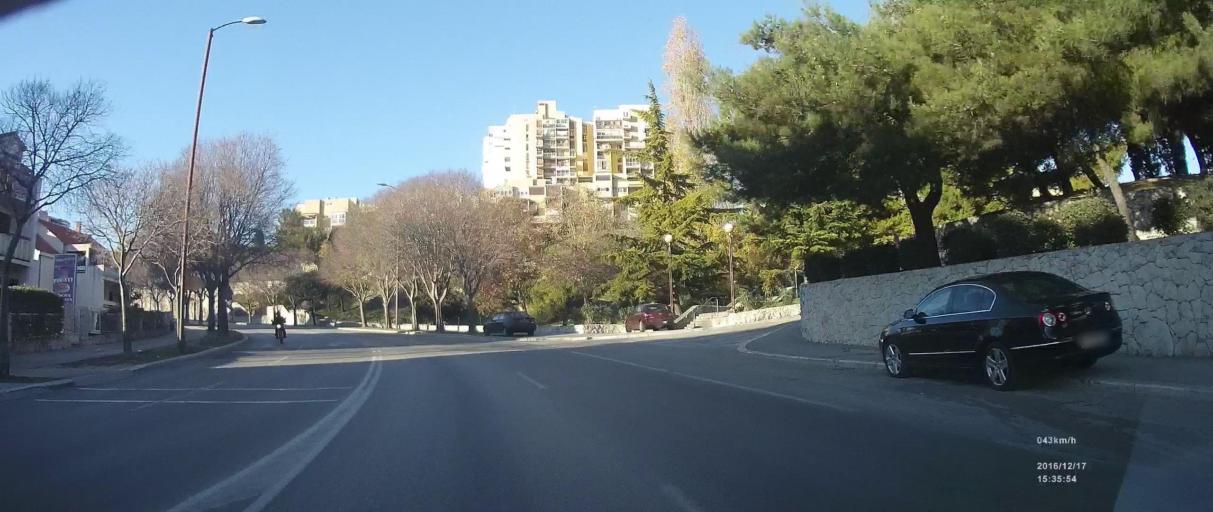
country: HR
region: Splitsko-Dalmatinska
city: Vranjic
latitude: 43.5067
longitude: 16.4789
